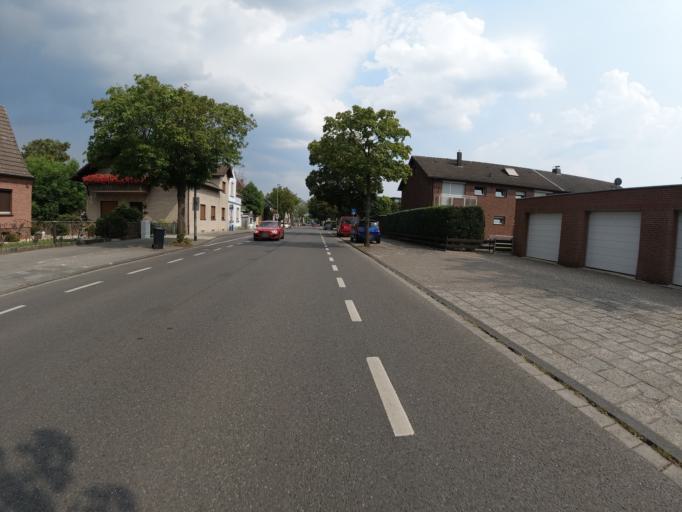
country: DE
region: North Rhine-Westphalia
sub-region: Regierungsbezirk Dusseldorf
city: Moers
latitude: 51.3922
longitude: 6.6464
